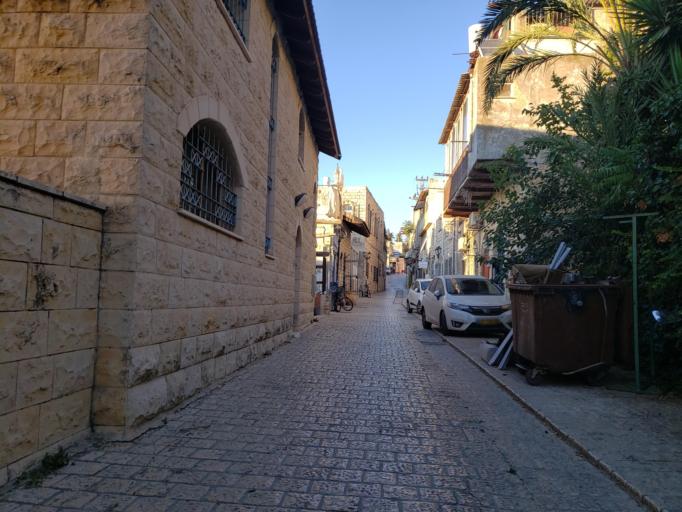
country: IL
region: Northern District
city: Safed
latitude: 32.9704
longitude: 35.4929
